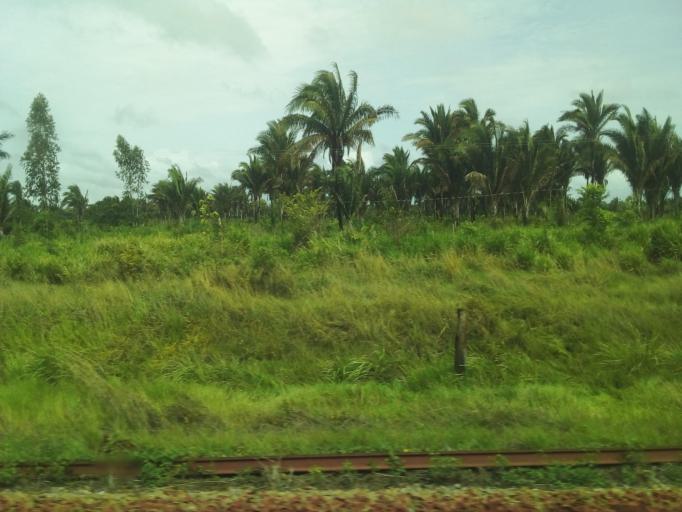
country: BR
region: Maranhao
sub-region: Arari
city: Arari
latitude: -3.5178
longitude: -44.6291
